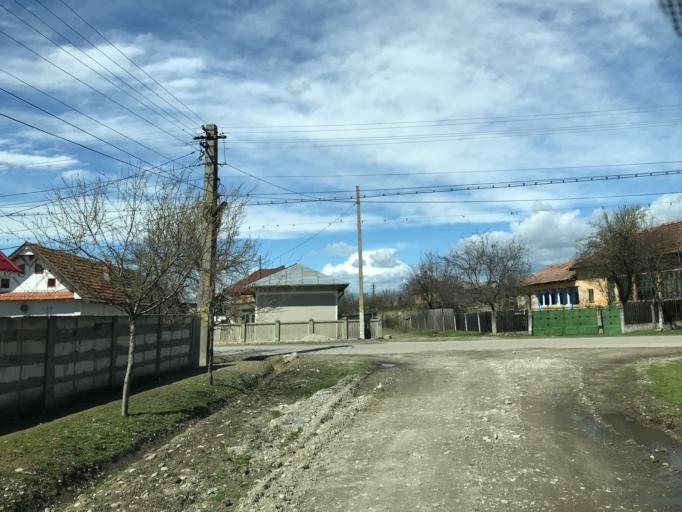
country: RO
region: Olt
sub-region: Comuna Osica de Sus
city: Osica de Sus
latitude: 44.2515
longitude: 24.3143
